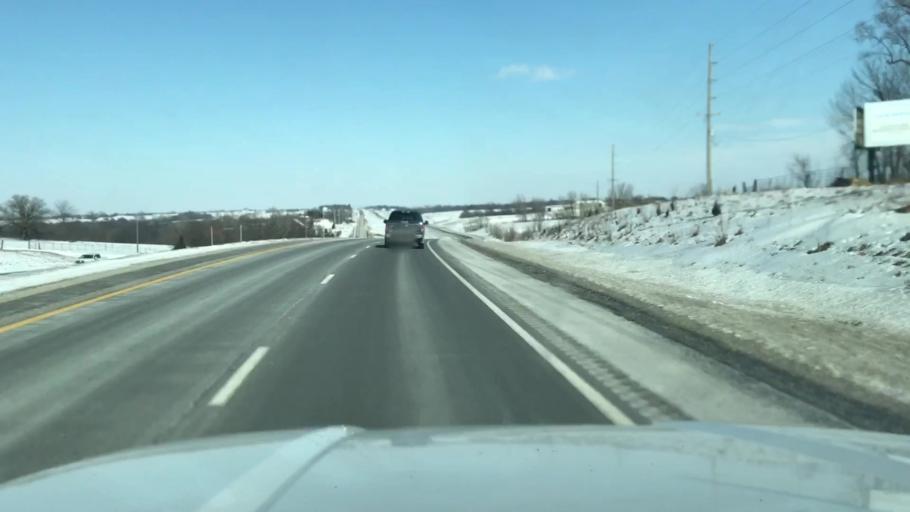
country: US
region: Missouri
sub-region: Nodaway County
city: Maryville
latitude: 40.1797
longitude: -94.8687
